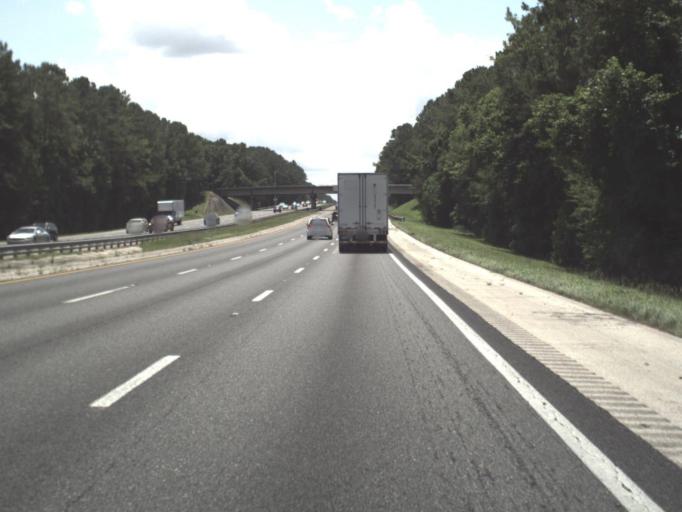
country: US
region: Florida
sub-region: Alachua County
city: Alachua
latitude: 29.7187
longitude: -82.4674
